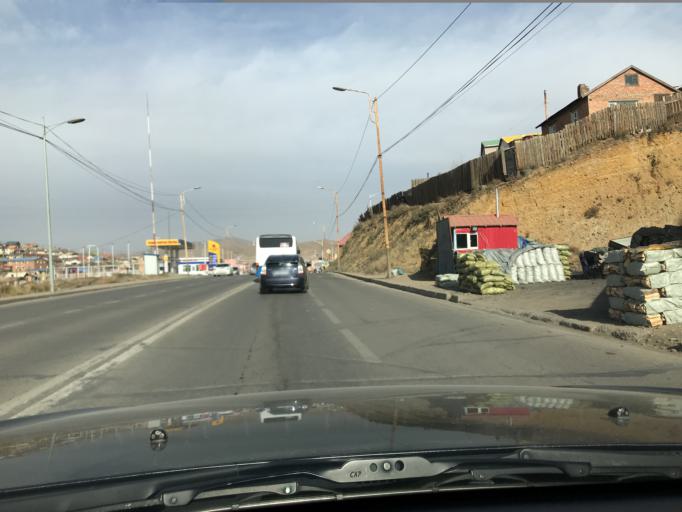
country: MN
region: Ulaanbaatar
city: Ulaanbaatar
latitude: 47.9361
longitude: 106.8842
